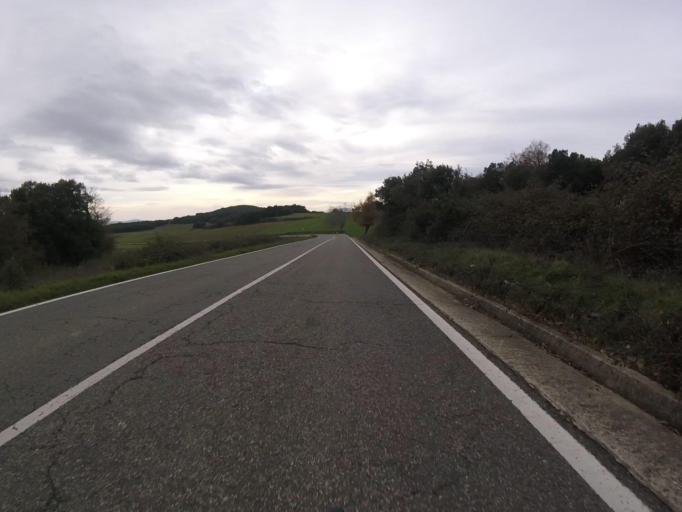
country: ES
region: Navarre
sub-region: Provincia de Navarra
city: Lezaun
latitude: 42.7415
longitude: -2.0209
